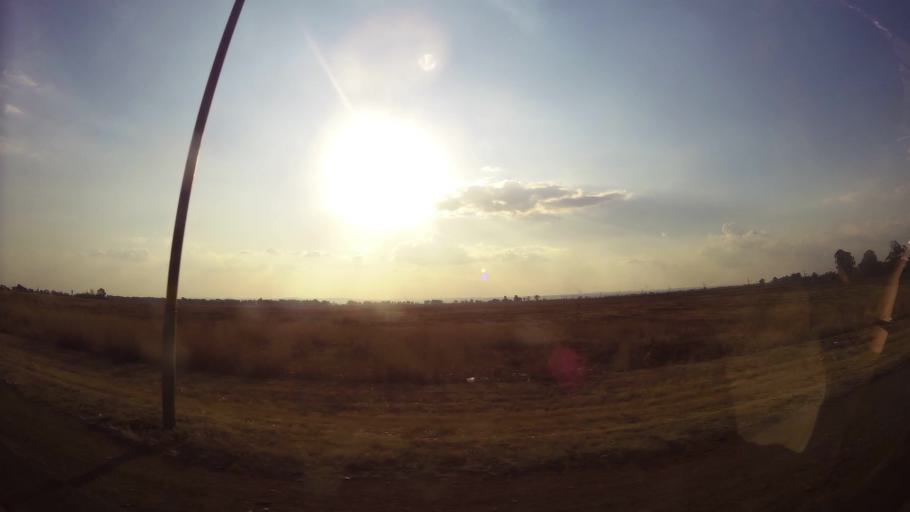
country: ZA
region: Gauteng
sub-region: Ekurhuleni Metropolitan Municipality
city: Germiston
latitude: -26.3306
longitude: 28.2358
